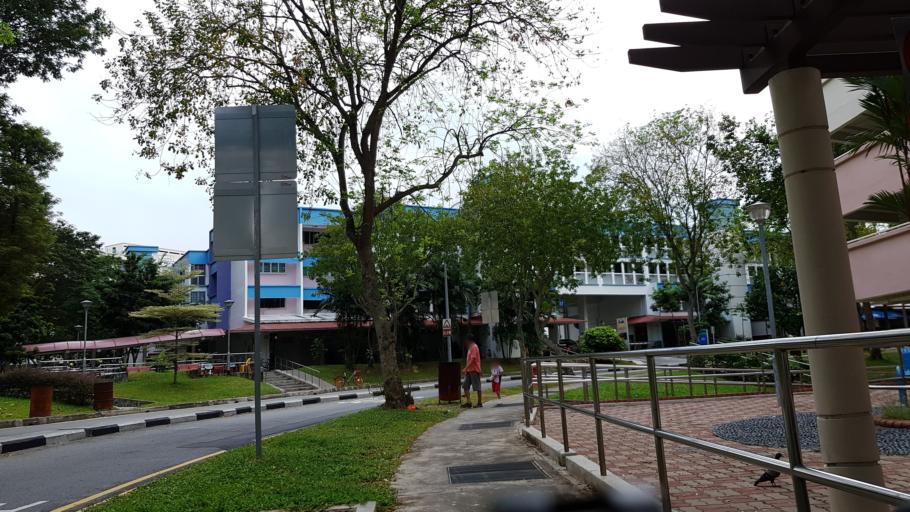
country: MY
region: Johor
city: Kampung Pasir Gudang Baru
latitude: 1.4365
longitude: 103.8389
